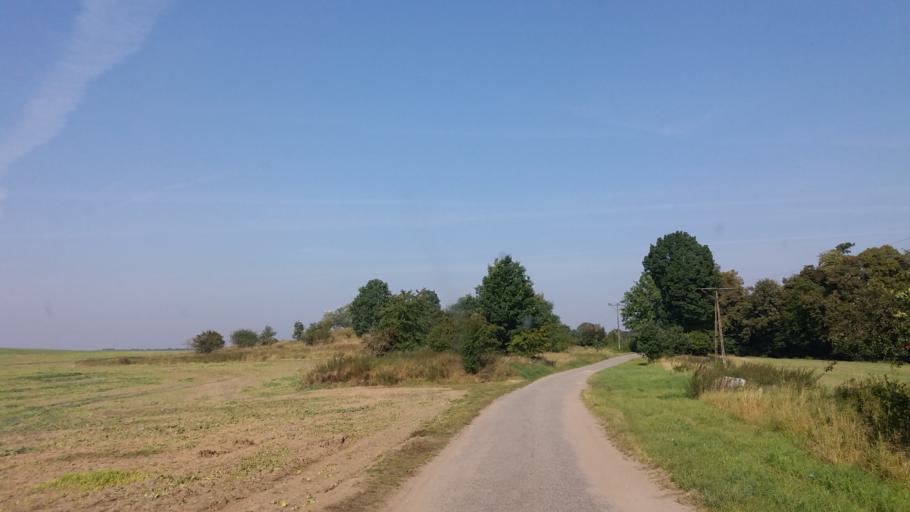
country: PL
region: West Pomeranian Voivodeship
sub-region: Powiat choszczenski
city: Pelczyce
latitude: 52.9776
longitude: 15.3383
